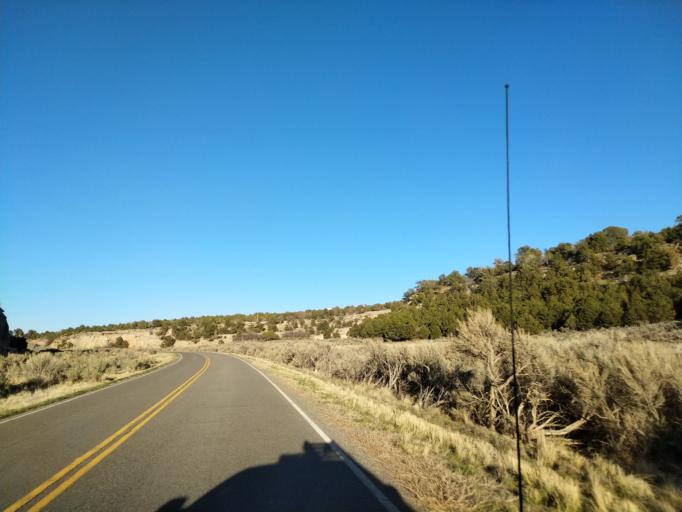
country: US
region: Colorado
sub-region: Mesa County
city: Redlands
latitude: 38.9885
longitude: -108.7796
